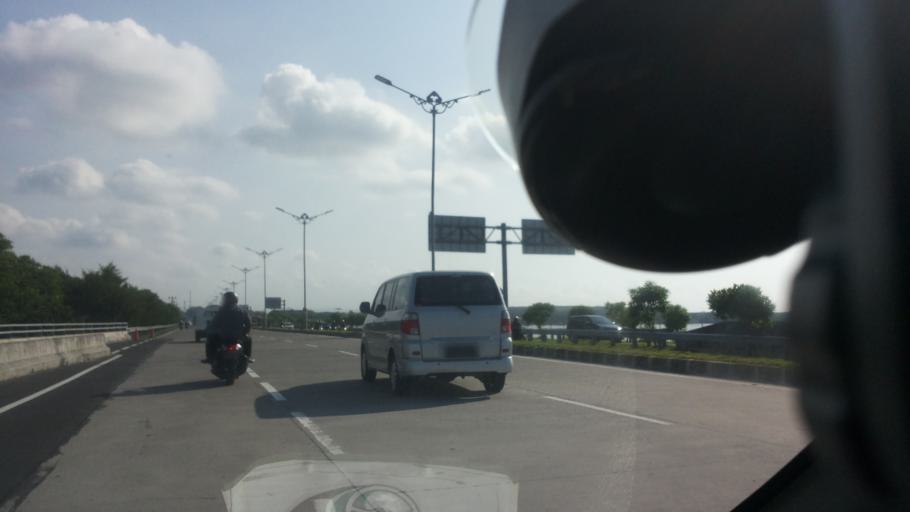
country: ID
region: Bali
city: Karyadharma
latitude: -8.7322
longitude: 115.2121
